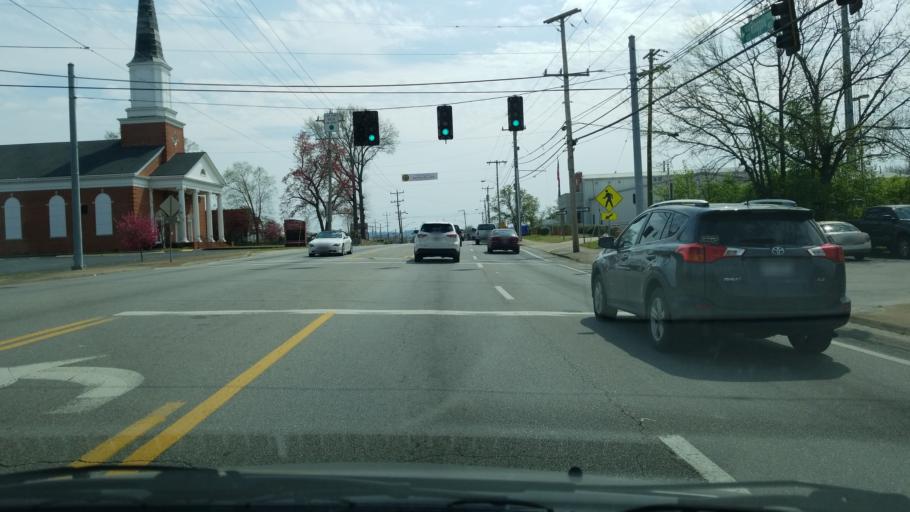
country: US
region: Tennessee
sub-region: Hamilton County
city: East Ridge
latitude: 34.9972
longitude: -85.2433
